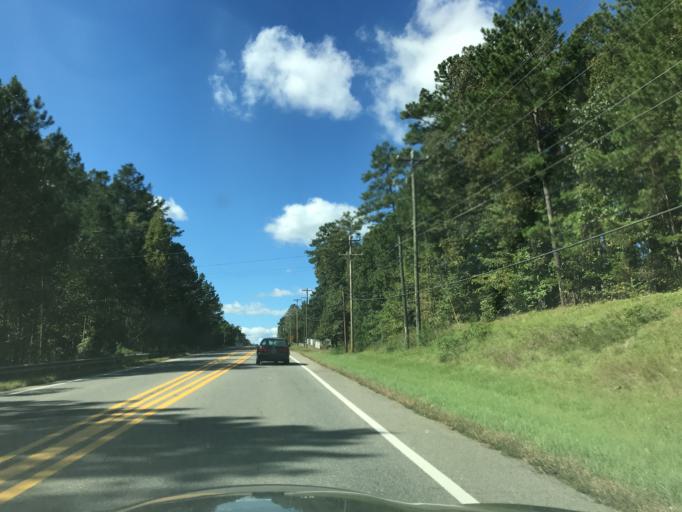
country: US
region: North Carolina
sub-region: Durham County
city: Gorman
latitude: 35.9776
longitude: -78.7734
